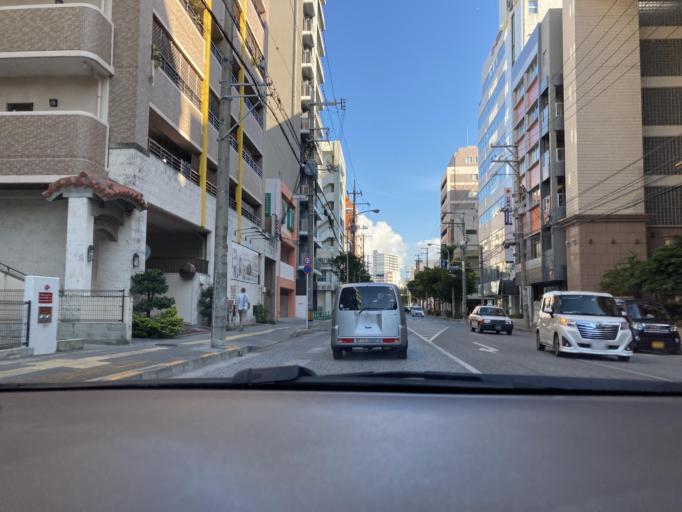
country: JP
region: Okinawa
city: Naha-shi
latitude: 26.2225
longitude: 127.6876
